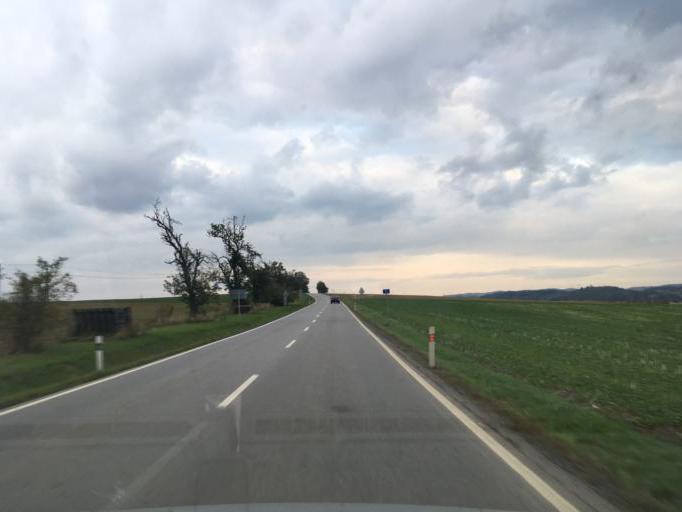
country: CZ
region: Vysocina
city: Starec
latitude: 49.2134
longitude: 15.8145
